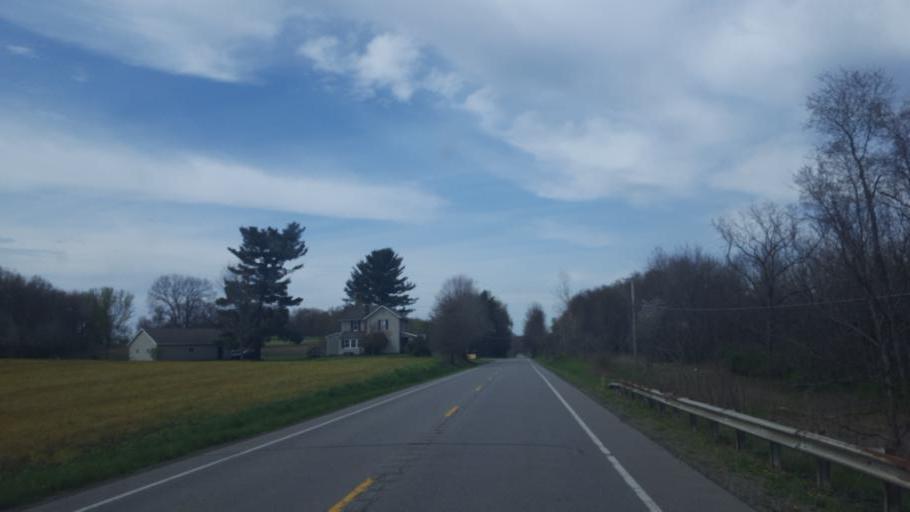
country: US
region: Pennsylvania
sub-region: Mercer County
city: Stoneboro
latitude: 41.3759
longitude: -80.0719
